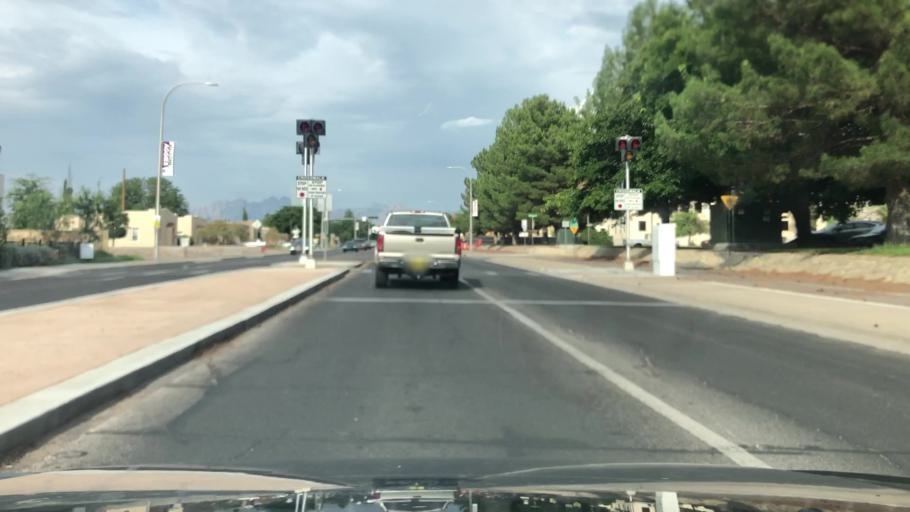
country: US
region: New Mexico
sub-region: Dona Ana County
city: University Park
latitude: 32.2844
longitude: -106.7545
